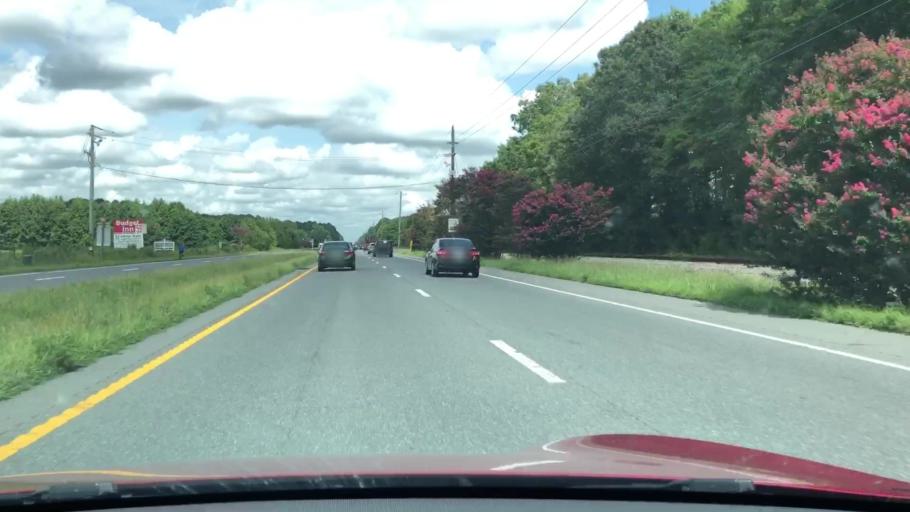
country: US
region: Virginia
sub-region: Northampton County
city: Exmore
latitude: 37.4824
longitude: -75.8535
